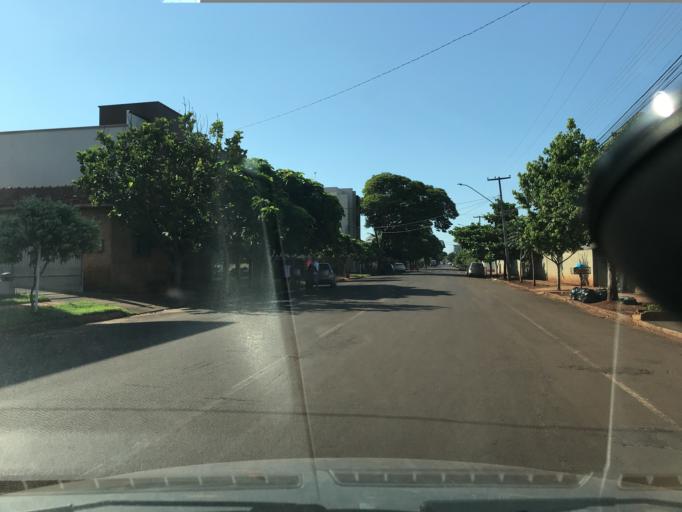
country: BR
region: Parana
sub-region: Palotina
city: Palotina
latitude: -24.2784
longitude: -53.8429
